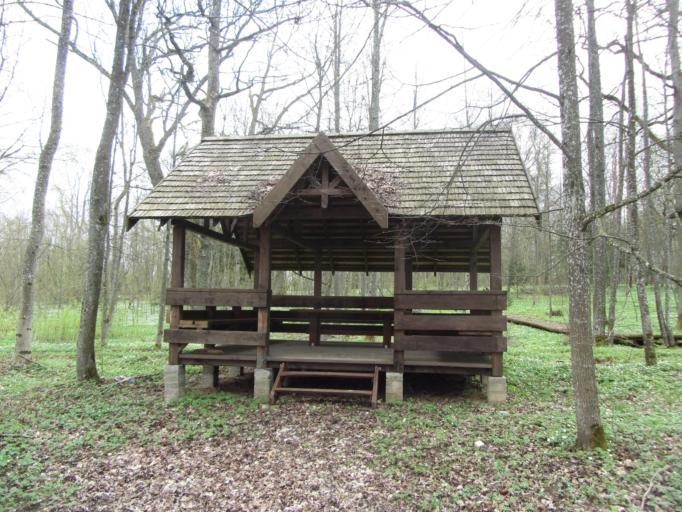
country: LT
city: Moletai
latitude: 55.1451
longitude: 25.4070
